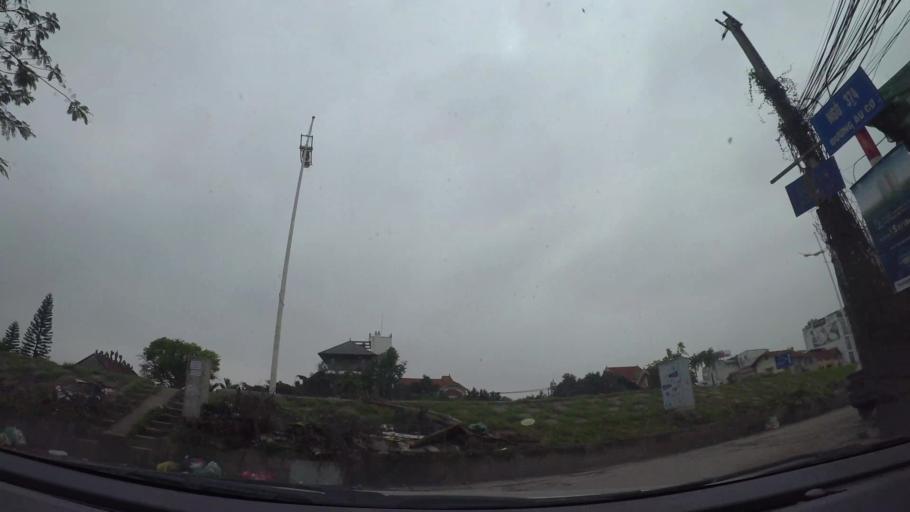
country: VN
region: Ha Noi
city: Tay Ho
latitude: 21.0772
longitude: 105.8221
